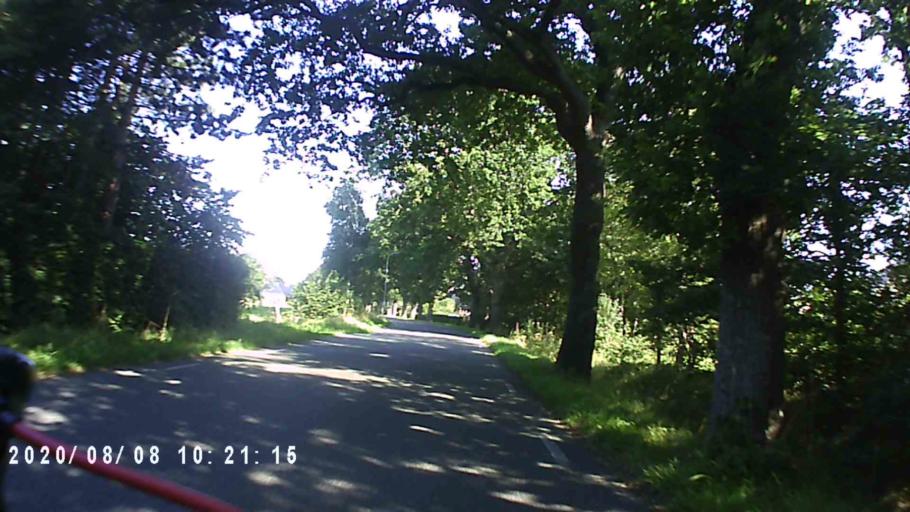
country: NL
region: Groningen
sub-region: Gemeente Leek
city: Leek
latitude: 53.1363
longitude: 6.3957
